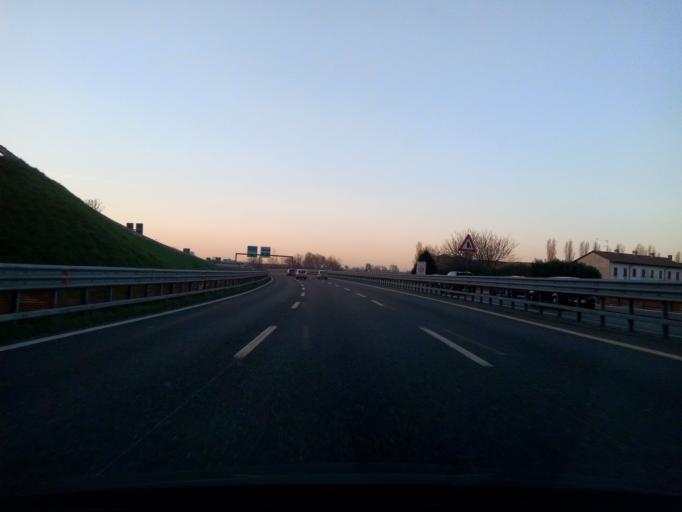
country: IT
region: Lombardy
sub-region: Citta metropolitana di Milano
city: Figino
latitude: 45.5080
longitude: 9.0636
